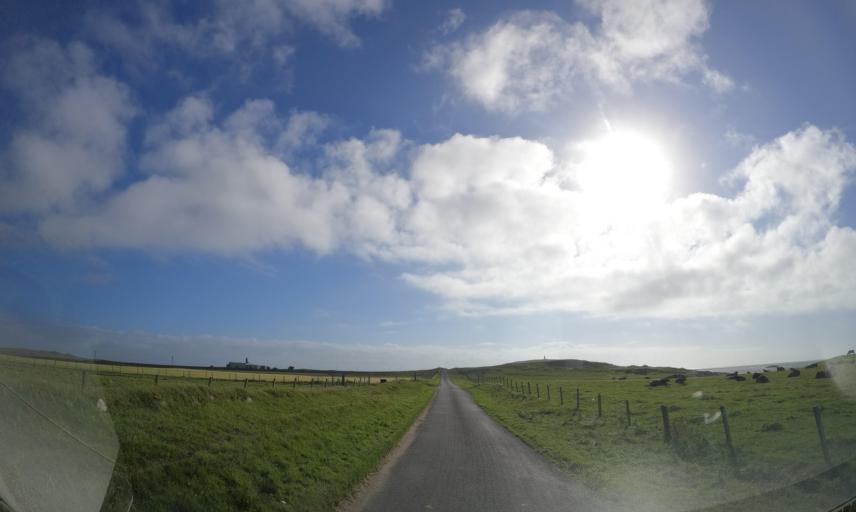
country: GB
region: Scotland
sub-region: Eilean Siar
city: Barra
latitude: 56.4925
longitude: -6.8434
